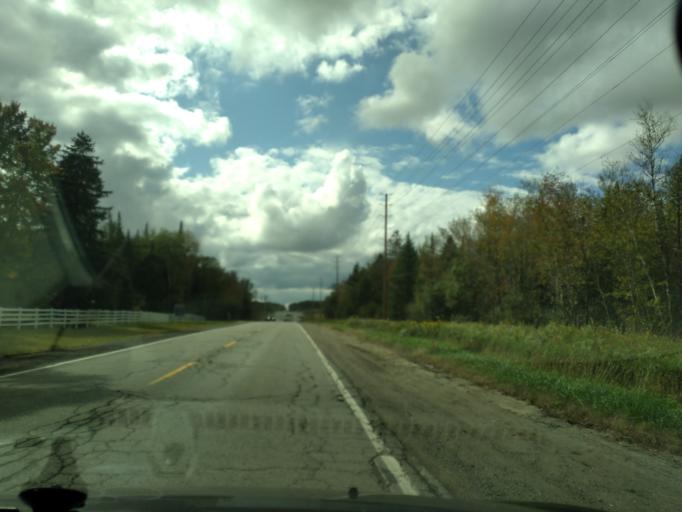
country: CA
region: Ontario
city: Innisfil
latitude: 44.2935
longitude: -79.6425
